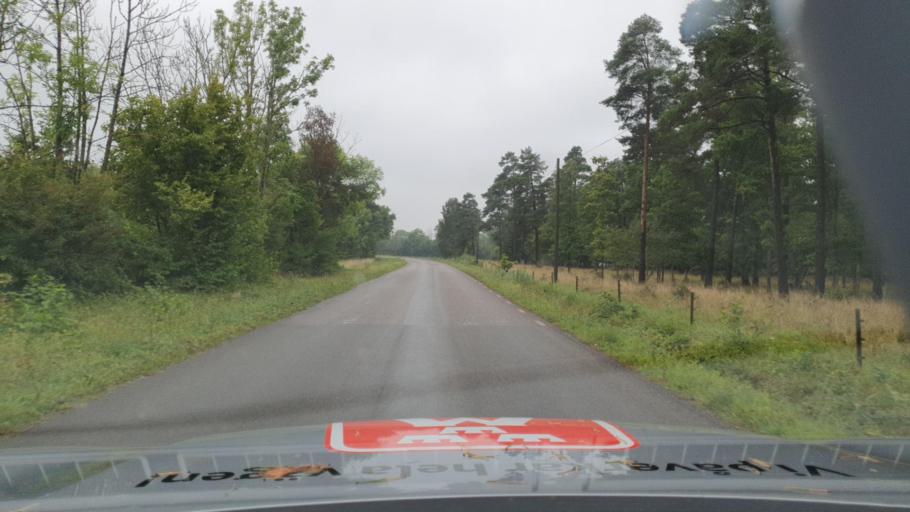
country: SE
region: Gotland
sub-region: Gotland
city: Visby
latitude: 57.7787
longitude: 18.5005
